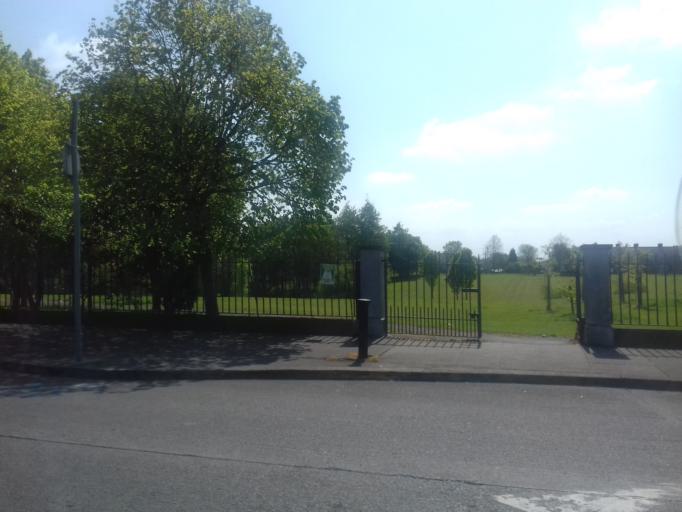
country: IE
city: Bonnybrook
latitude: 53.3975
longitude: -6.2064
